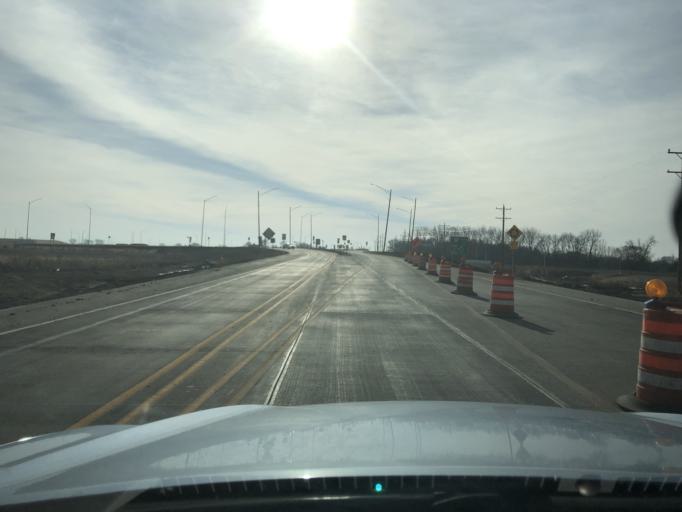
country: US
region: Illinois
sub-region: McHenry County
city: Marengo
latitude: 42.1809
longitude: -88.6180
